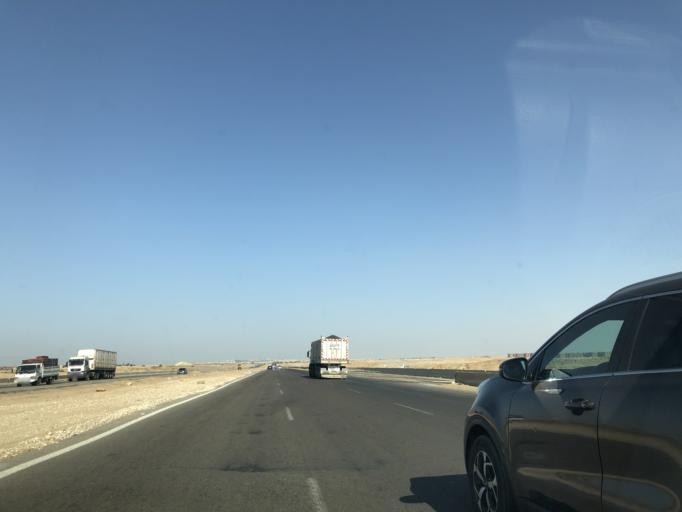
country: EG
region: Muhafazat al Minufiyah
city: Ashmun
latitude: 30.0677
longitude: 30.8708
